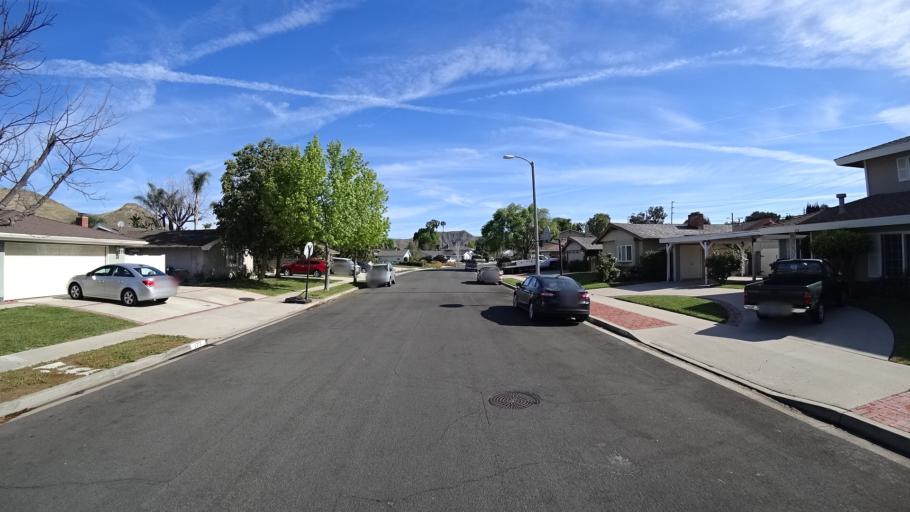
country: US
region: California
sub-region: Ventura County
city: Casa Conejo
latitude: 34.1744
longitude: -118.9548
